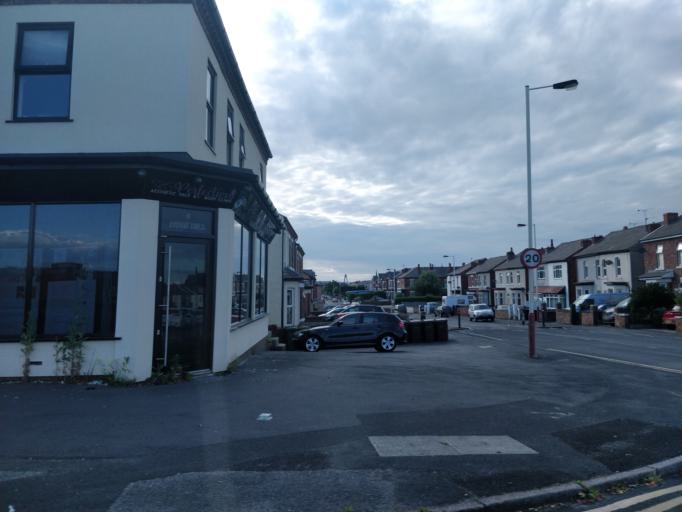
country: GB
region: England
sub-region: Sefton
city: Southport
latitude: 53.6440
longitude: -2.9888
